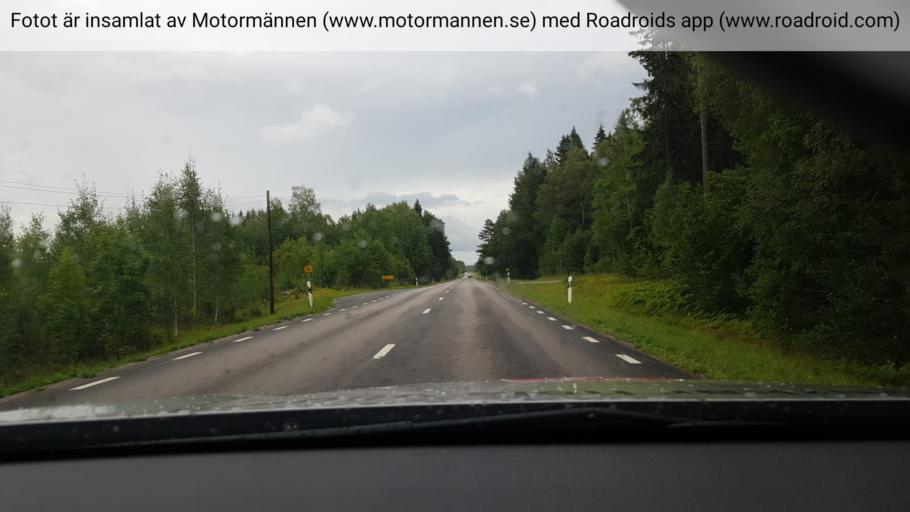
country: SE
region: Uppsala
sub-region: Tierps Kommun
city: Karlholmsbruk
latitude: 60.5429
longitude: 17.5441
